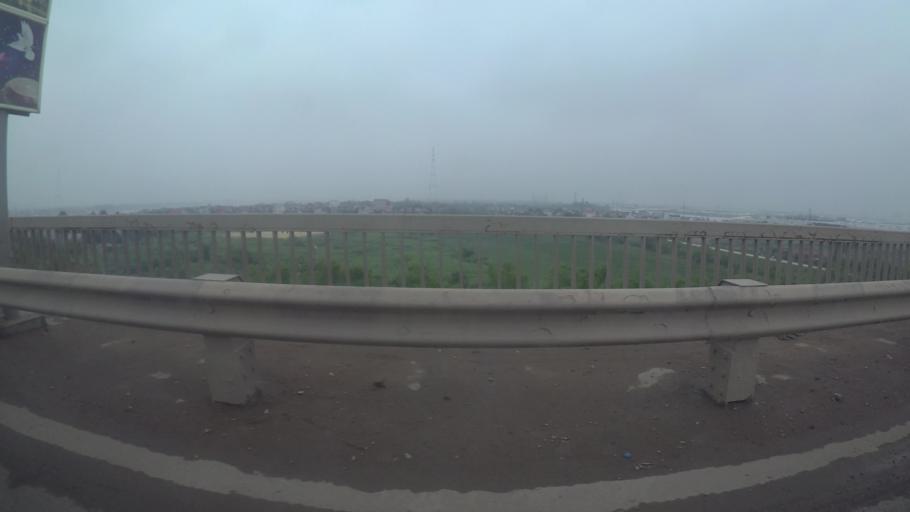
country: VN
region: Ha Noi
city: Tay Ho
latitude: 21.1048
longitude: 105.7868
